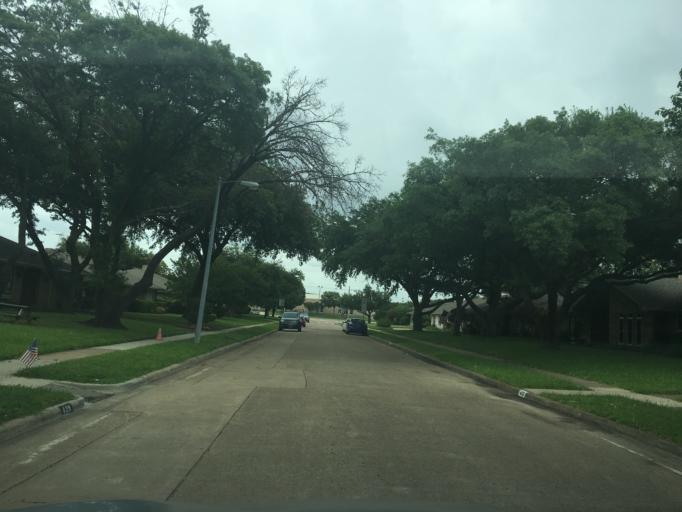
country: US
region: Texas
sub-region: Dallas County
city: Richardson
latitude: 32.9323
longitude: -96.7295
